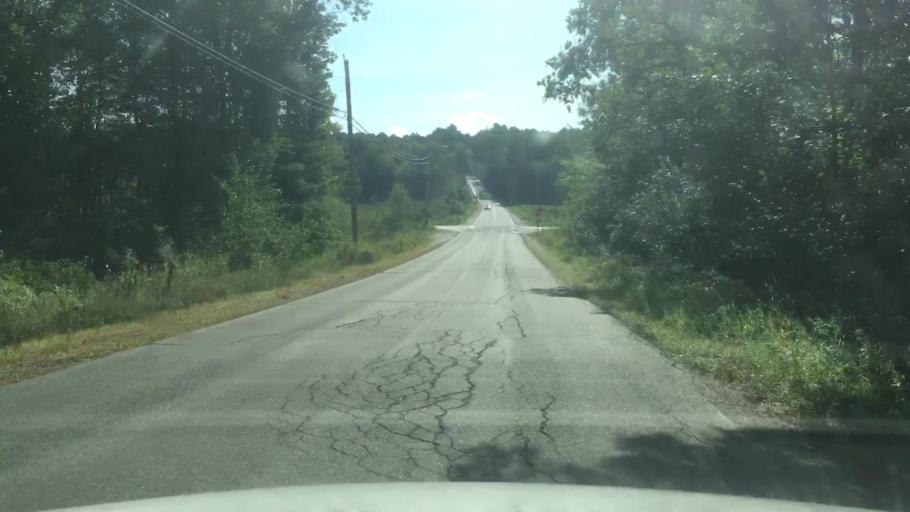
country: US
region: Maine
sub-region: Kennebec County
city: Gardiner
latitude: 44.1647
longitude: -69.8103
